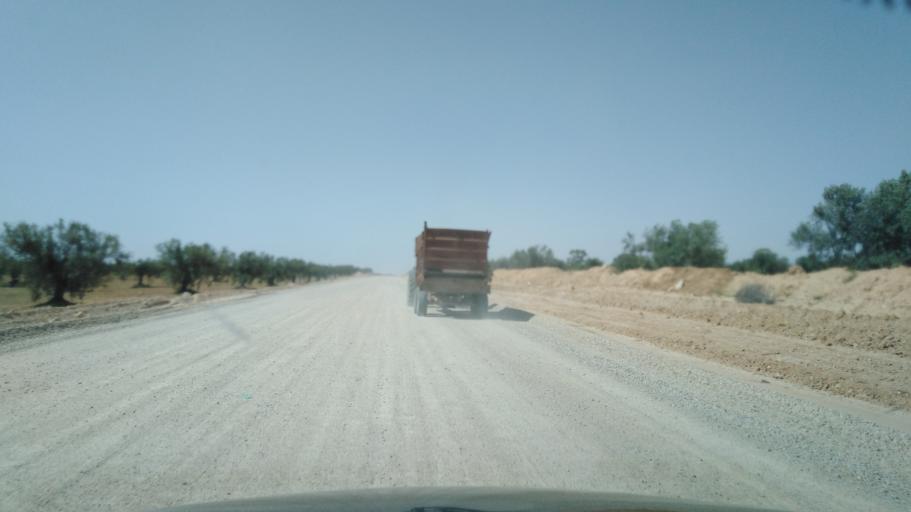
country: TN
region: Safaqis
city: Sfax
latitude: 34.7137
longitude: 10.5006
